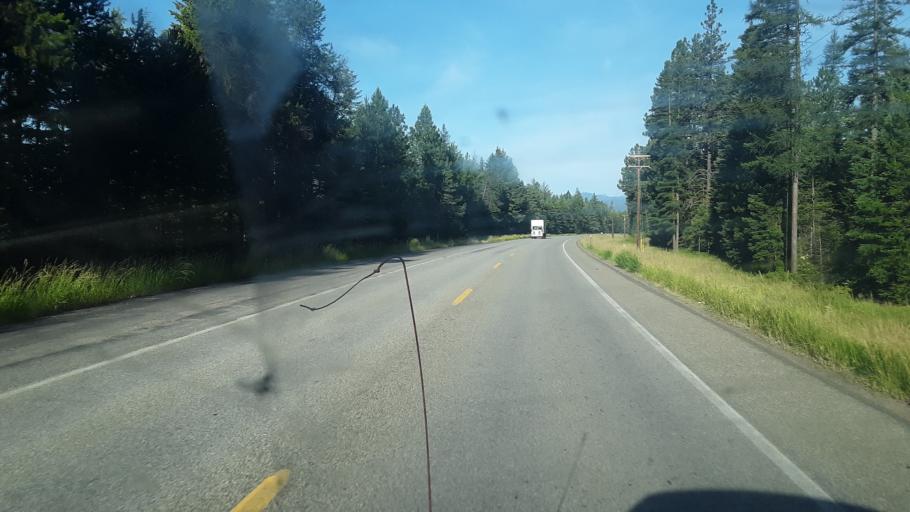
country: US
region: Idaho
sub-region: Boundary County
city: Bonners Ferry
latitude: 48.7278
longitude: -116.2003
